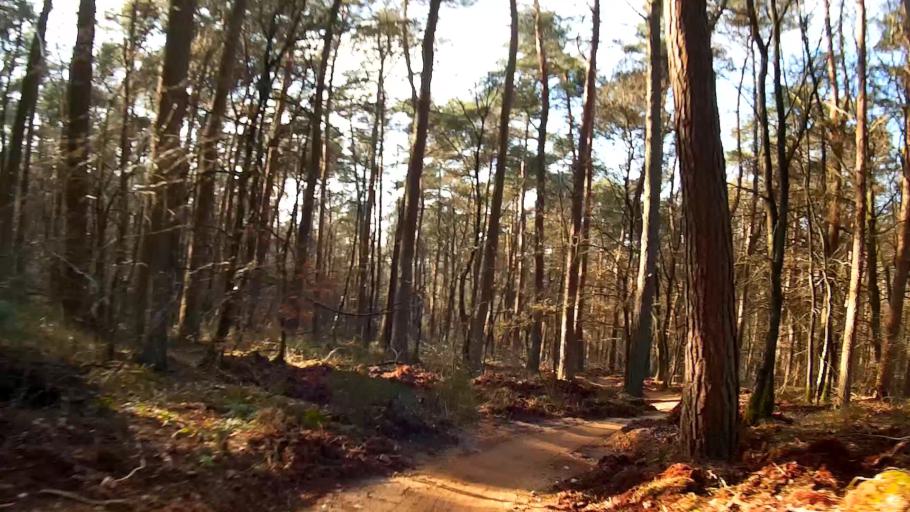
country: NL
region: Utrecht
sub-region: Gemeente Utrechtse Heuvelrug
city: Amerongen
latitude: 52.0203
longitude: 5.4690
